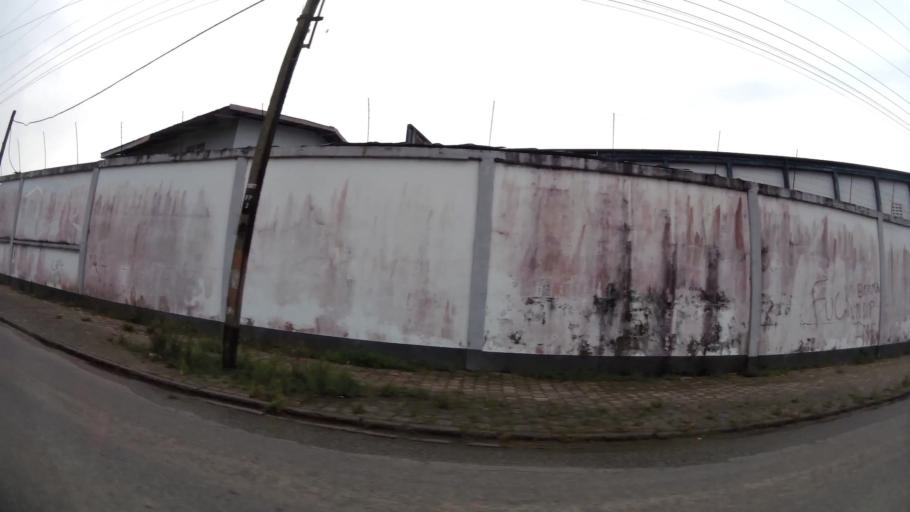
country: SR
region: Paramaribo
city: Paramaribo
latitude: 5.8224
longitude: -55.2034
